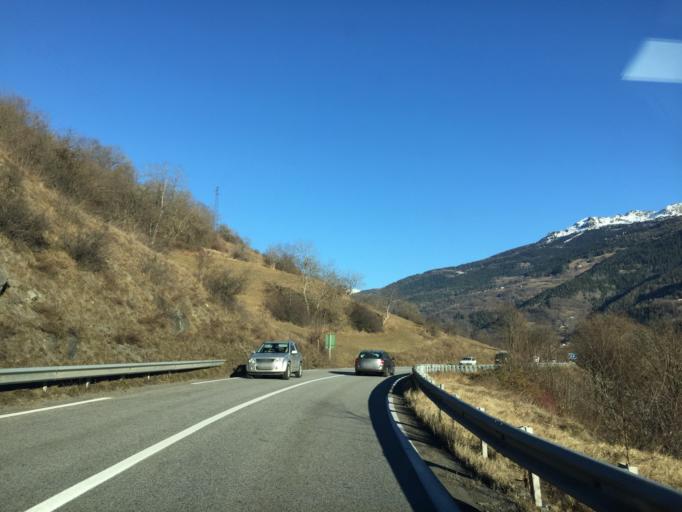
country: FR
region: Rhone-Alpes
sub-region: Departement de la Savoie
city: Macot-la-Plagne
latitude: 45.5731
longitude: 6.7233
